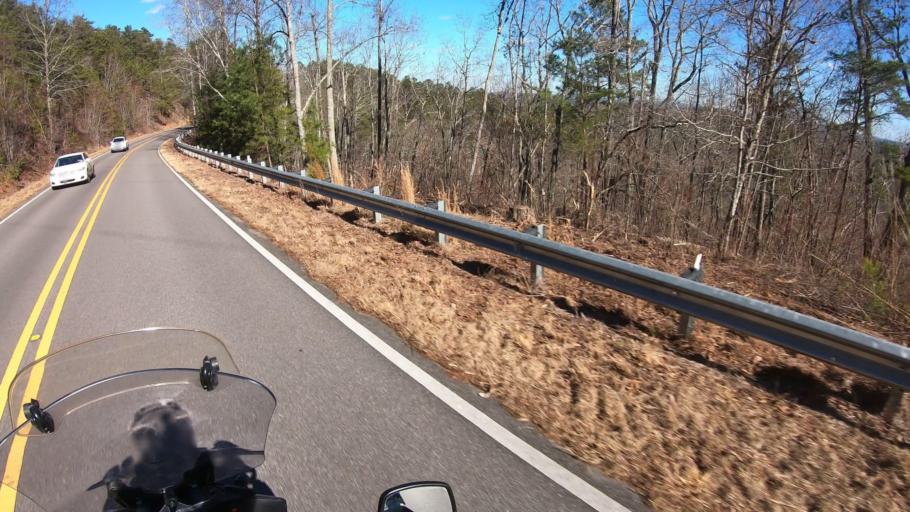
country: US
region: Alabama
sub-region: Calhoun County
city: Oxford
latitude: 33.5203
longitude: -85.7522
